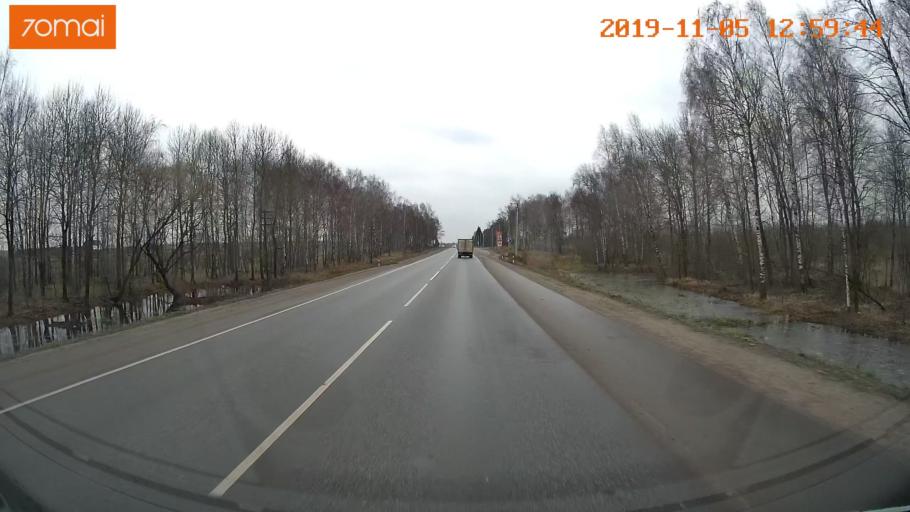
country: RU
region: Ivanovo
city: Kokhma
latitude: 56.9170
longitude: 41.1341
